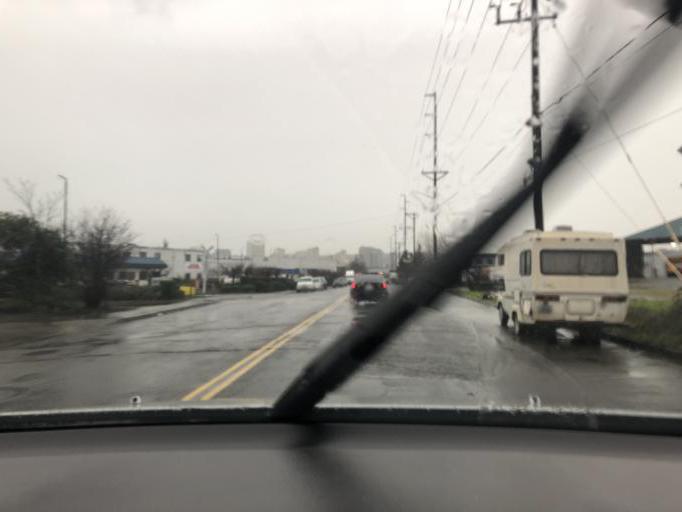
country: US
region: Washington
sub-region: Pierce County
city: Tacoma
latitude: 47.2502
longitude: -122.4182
